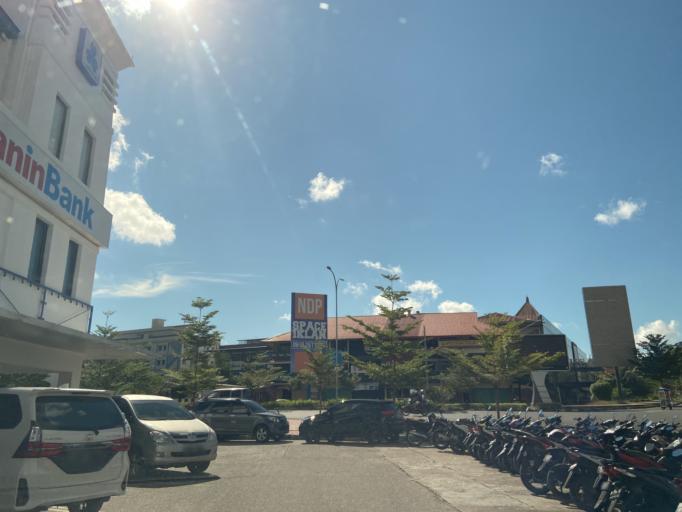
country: SG
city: Singapore
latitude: 1.1487
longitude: 104.0118
